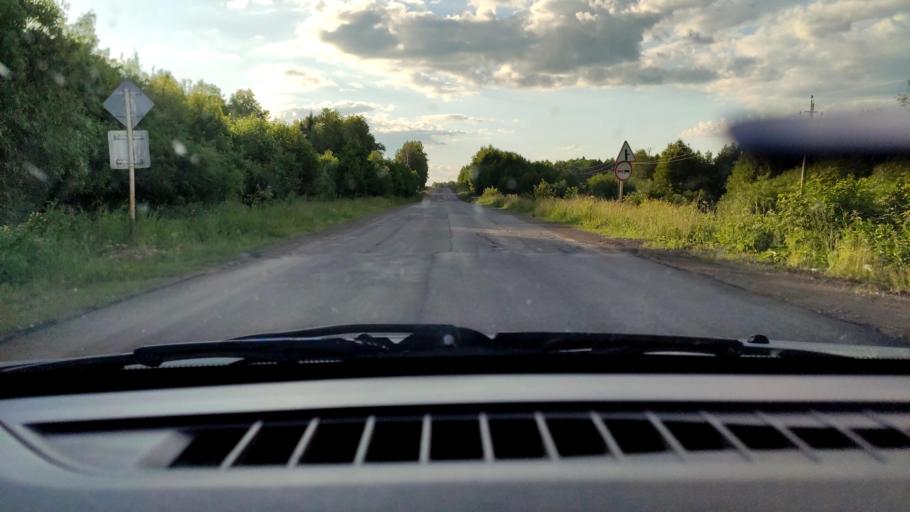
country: RU
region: Perm
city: Uinskoye
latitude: 57.0885
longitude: 56.5576
